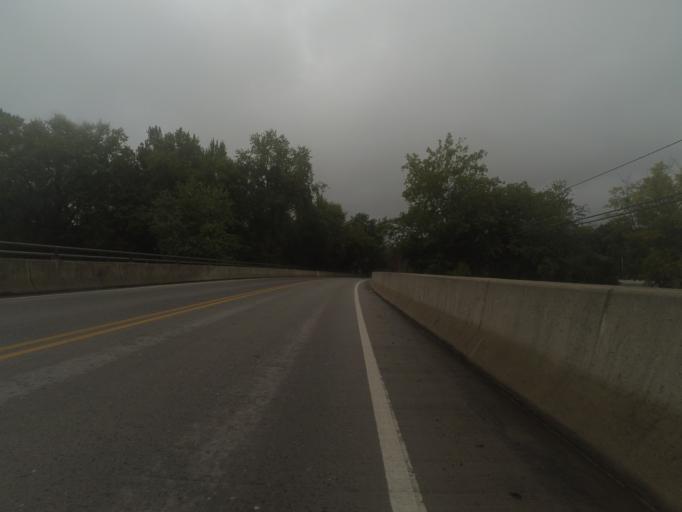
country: US
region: Pennsylvania
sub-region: Huntingdon County
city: McConnellstown
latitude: 40.5556
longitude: -78.0988
